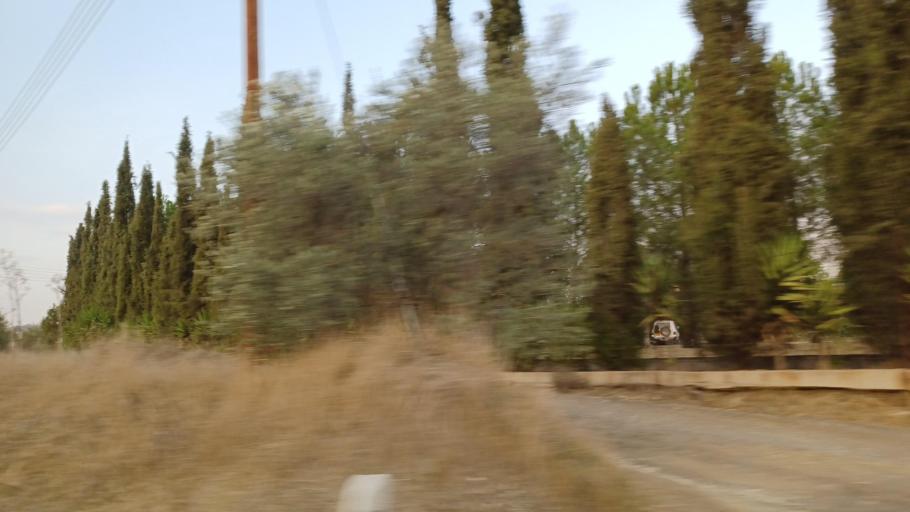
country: CY
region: Larnaka
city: Mosfiloti
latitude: 34.9446
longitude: 33.4148
